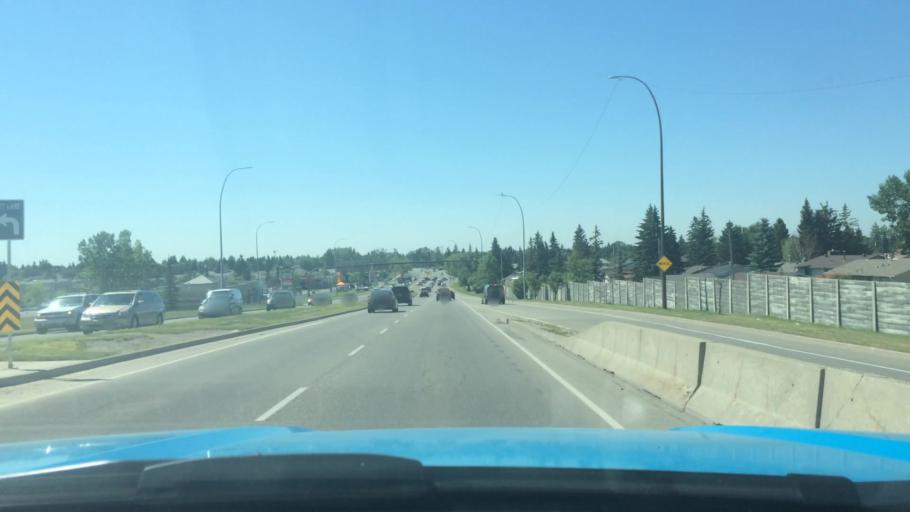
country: CA
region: Alberta
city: Calgary
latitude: 51.0658
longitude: -113.9585
